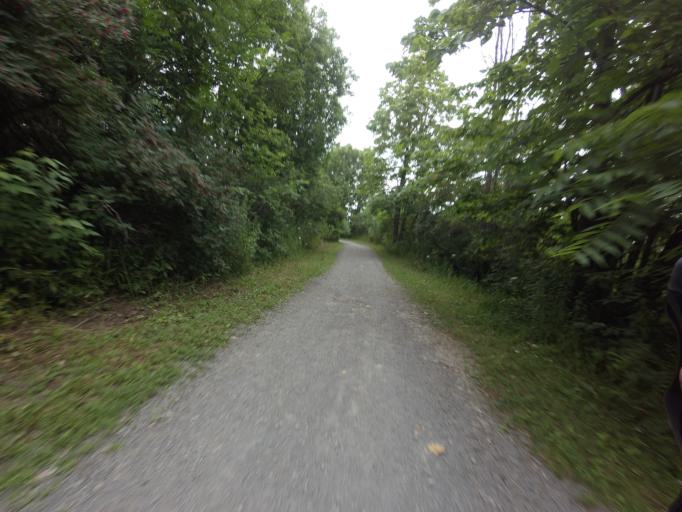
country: CA
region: Ontario
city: Bells Corners
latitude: 45.2542
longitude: -75.7064
